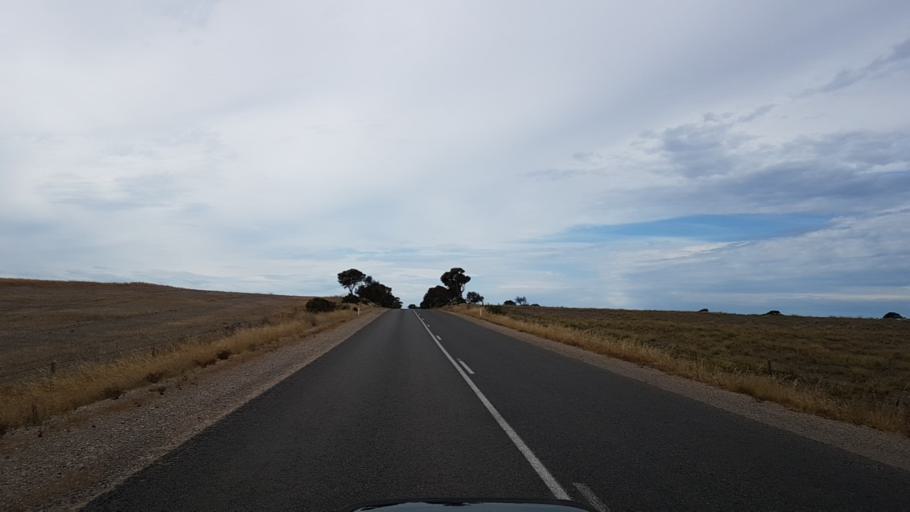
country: AU
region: South Australia
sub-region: Yorke Peninsula
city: Honiton
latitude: -34.9429
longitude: 137.0943
